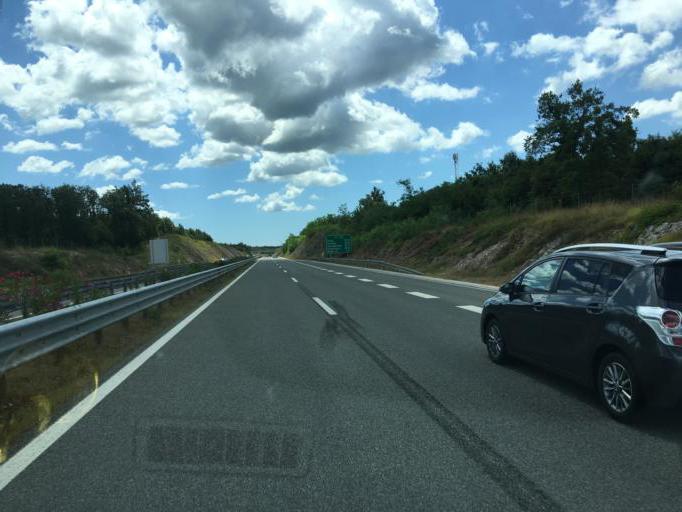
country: HR
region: Istarska
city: Karojba
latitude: 45.2123
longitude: 13.7252
